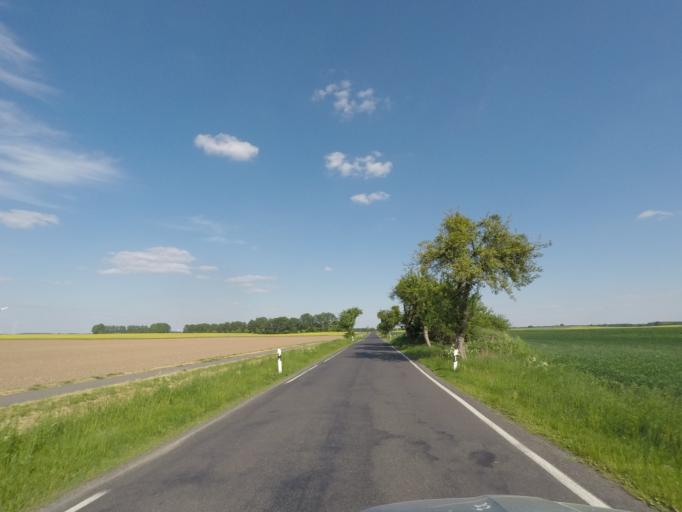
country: DE
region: Brandenburg
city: Werftpfuhl
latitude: 52.7345
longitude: 13.8508
